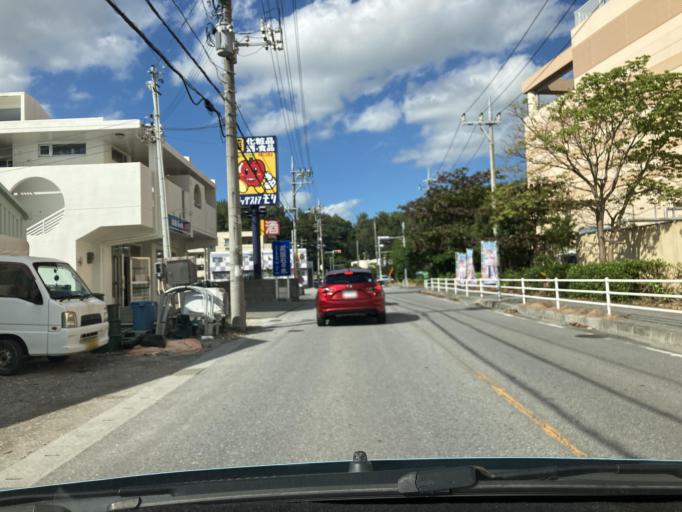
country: JP
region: Okinawa
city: Katsuren-haebaru
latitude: 26.3377
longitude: 127.8434
